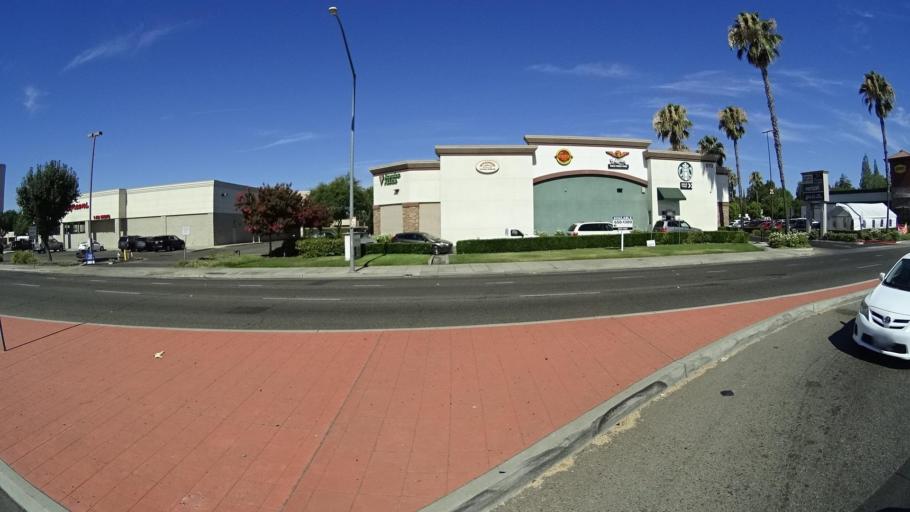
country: US
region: California
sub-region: Fresno County
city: Sunnyside
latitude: 36.7370
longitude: -119.7000
